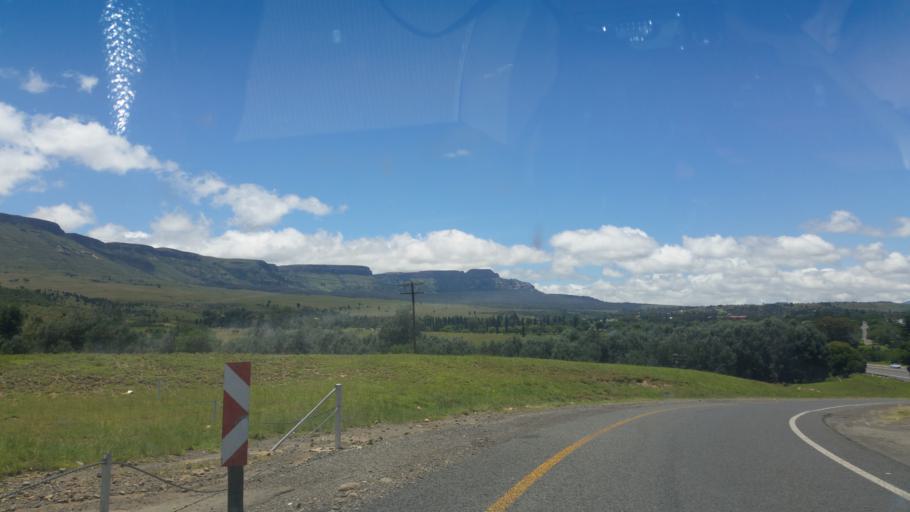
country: ZA
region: Orange Free State
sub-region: Thabo Mofutsanyana District Municipality
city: Harrismith
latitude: -28.2584
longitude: 29.1184
